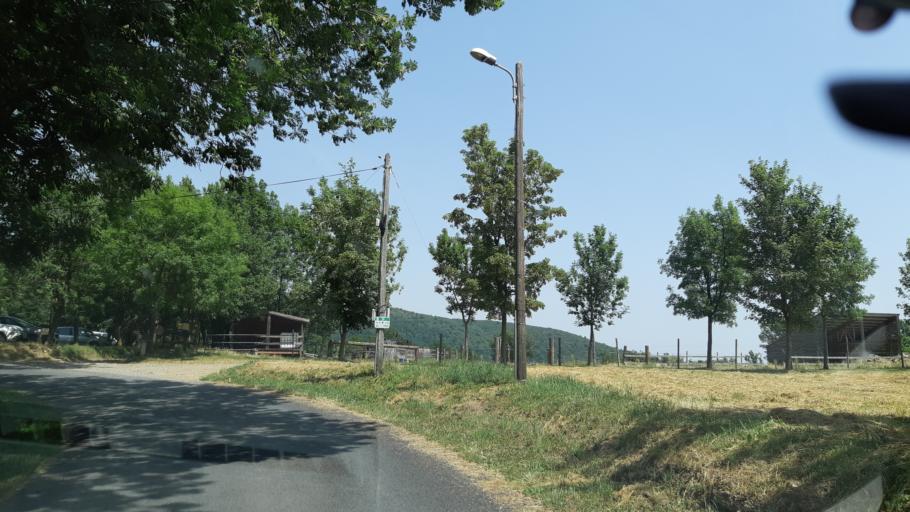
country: FR
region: Languedoc-Roussillon
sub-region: Departement des Pyrenees-Orientales
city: Arles
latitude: 42.5471
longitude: 2.5874
